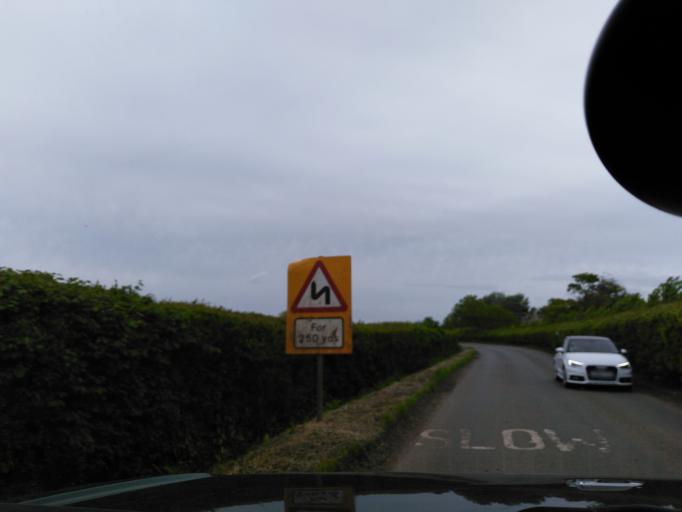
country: GB
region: England
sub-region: Wiltshire
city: Corsham
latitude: 51.4281
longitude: -2.1561
